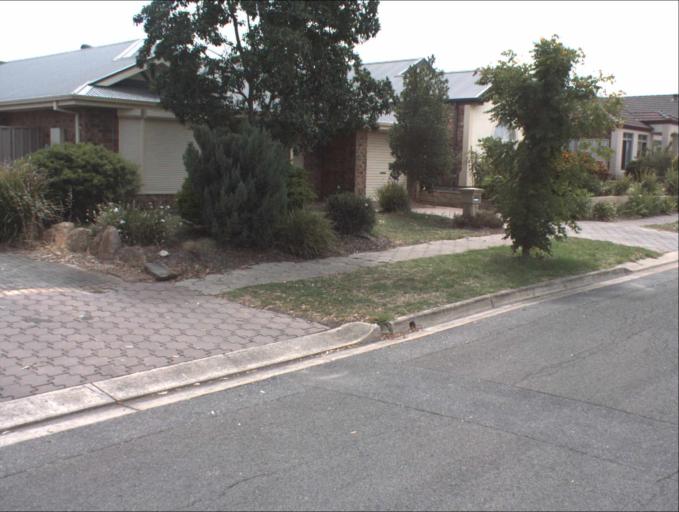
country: AU
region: South Australia
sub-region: Port Adelaide Enfield
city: Gilles Plains
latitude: -34.8587
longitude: 138.6604
